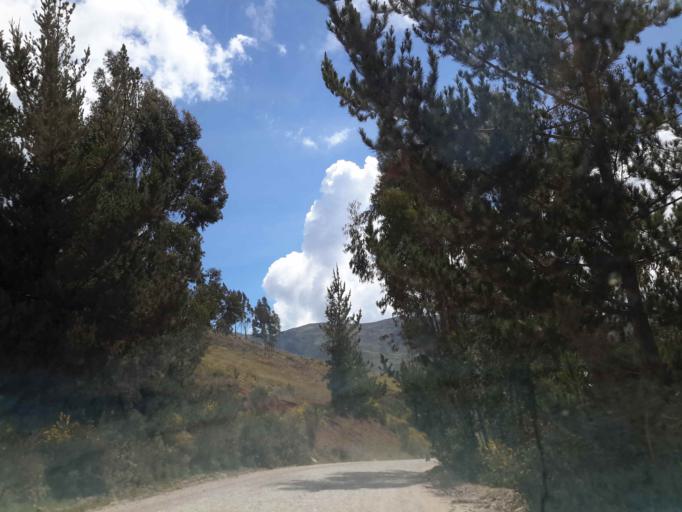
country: PE
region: Apurimac
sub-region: Provincia de Andahuaylas
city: Pacucha
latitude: -13.6252
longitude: -73.3379
